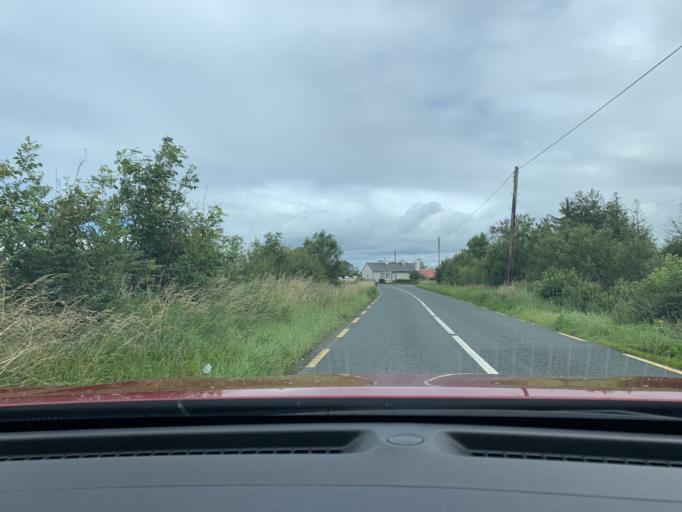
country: IE
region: Connaught
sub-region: County Leitrim
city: Carrick-on-Shannon
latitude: 53.8984
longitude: -8.1378
